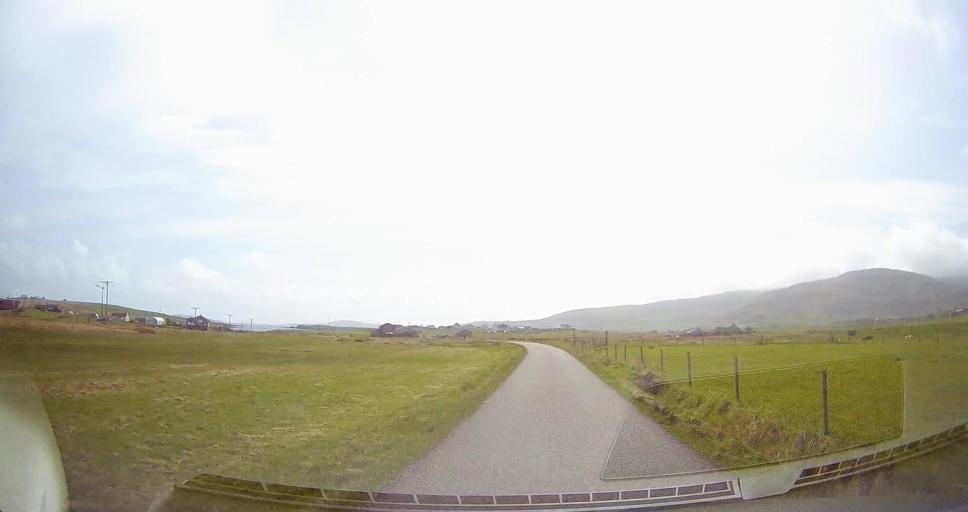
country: GB
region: Scotland
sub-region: Shetland Islands
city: Sandwick
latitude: 60.0470
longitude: -1.2156
